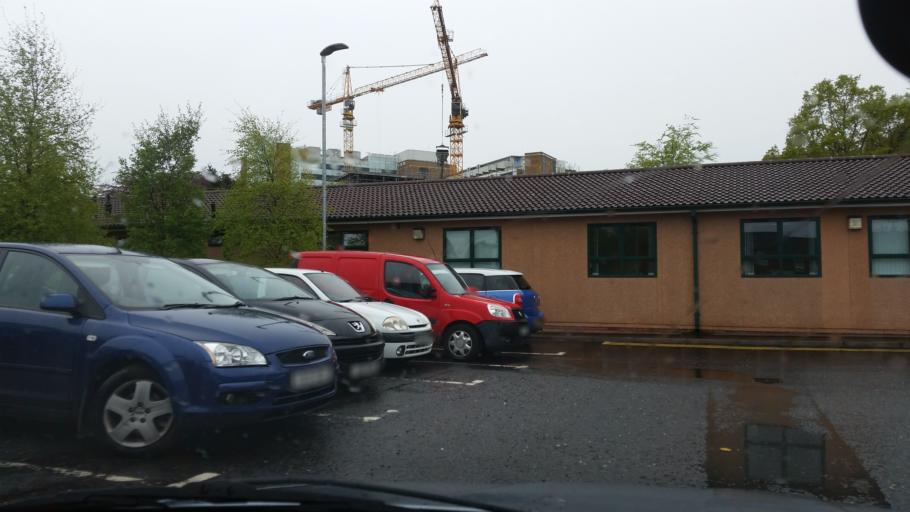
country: GB
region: Northern Ireland
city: Londonderry County Borough
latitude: 54.9880
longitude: -7.2922
